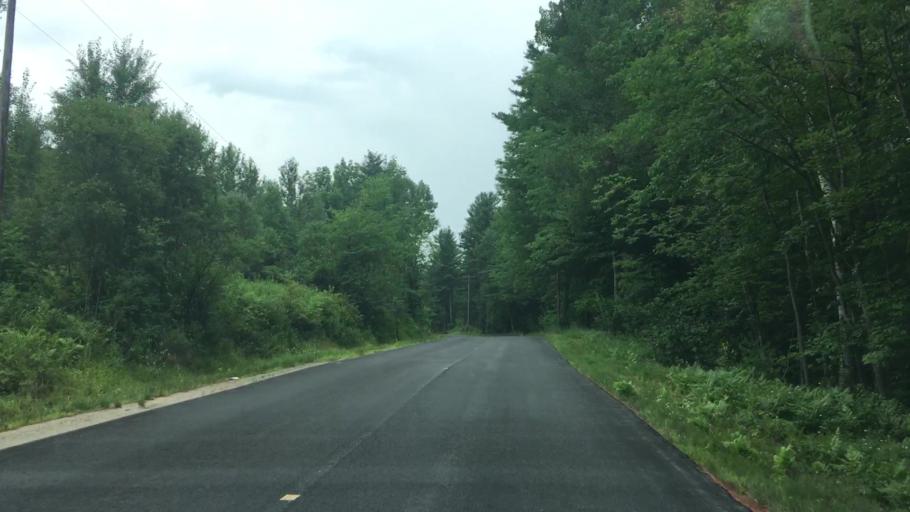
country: US
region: New York
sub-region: Essex County
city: Keeseville
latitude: 44.4296
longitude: -73.6274
